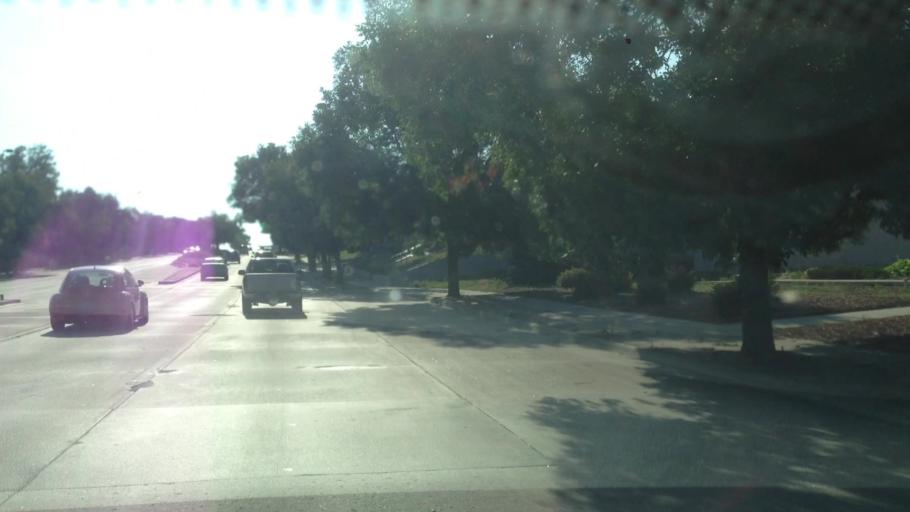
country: US
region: Colorado
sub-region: Jefferson County
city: Lakewood
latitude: 39.7113
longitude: -105.0492
